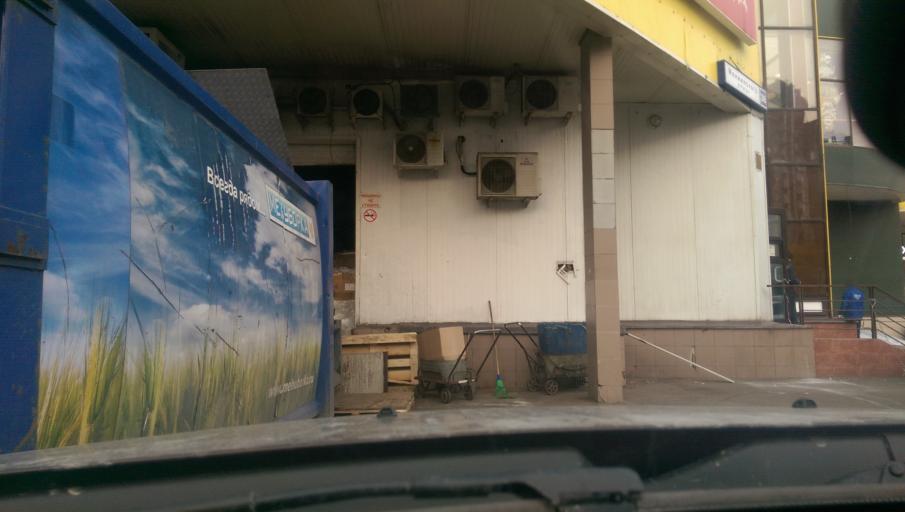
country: RU
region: Moscow
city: Leonovo
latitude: 55.8703
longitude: 37.6626
